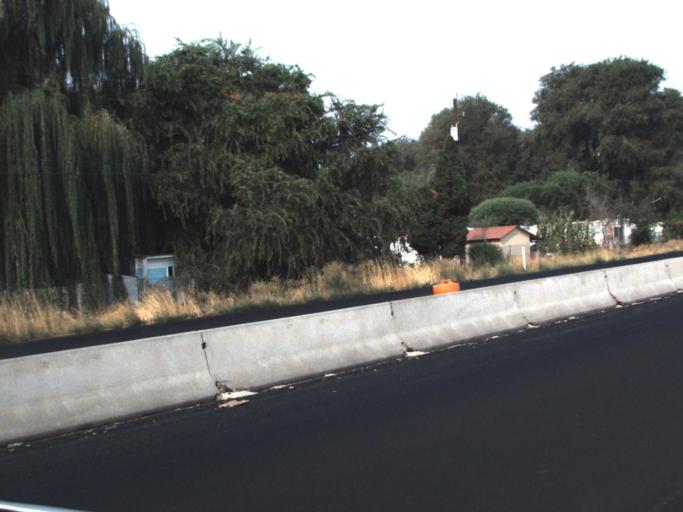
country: US
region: Washington
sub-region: Yakima County
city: Toppenish
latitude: 46.3942
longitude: -120.3649
